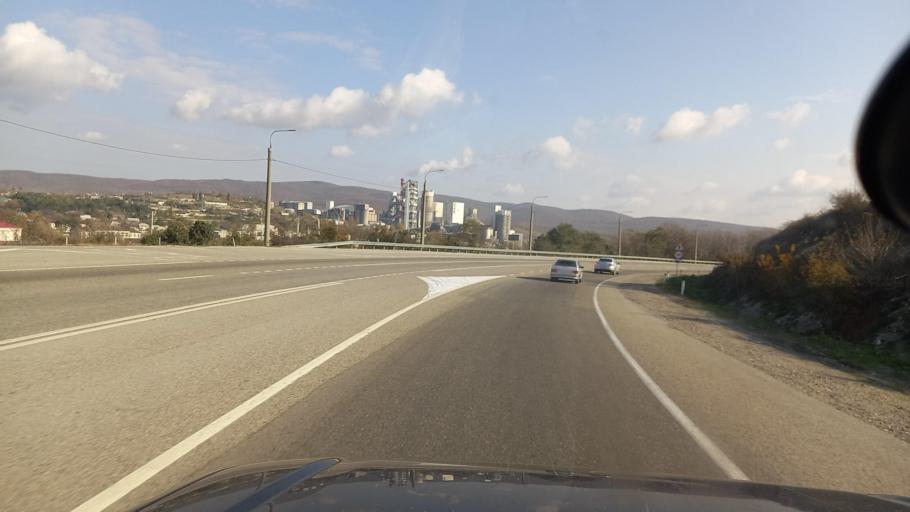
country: RU
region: Krasnodarskiy
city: Verkhnebakanskiy
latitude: 44.8360
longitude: 37.6589
